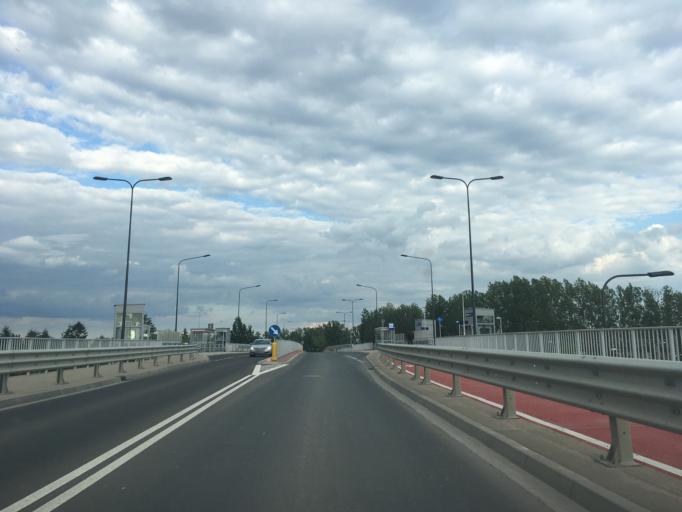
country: PL
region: Masovian Voivodeship
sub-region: Powiat piaseczynski
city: Mysiadlo
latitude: 52.1105
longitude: 20.9923
